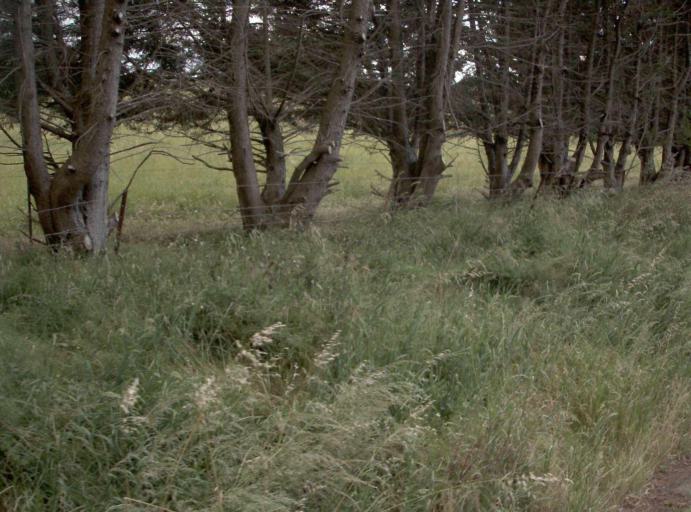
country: AU
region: Victoria
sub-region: Baw Baw
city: Warragul
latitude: -38.0988
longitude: 145.9219
